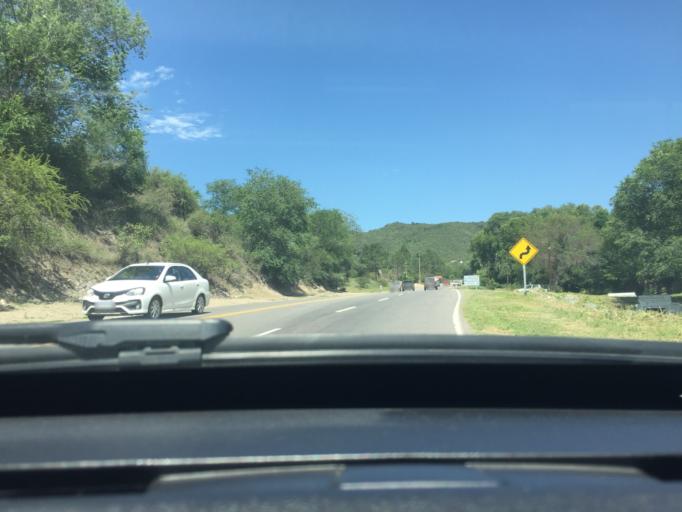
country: AR
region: Cordoba
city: Alta Gracia
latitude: -31.7411
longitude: -64.4554
